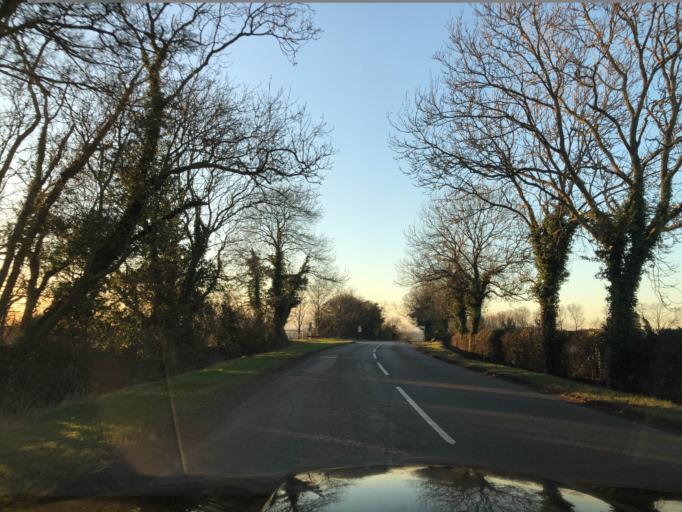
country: GB
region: England
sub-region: Warwickshire
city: Harbury
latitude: 52.2327
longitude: -1.4852
